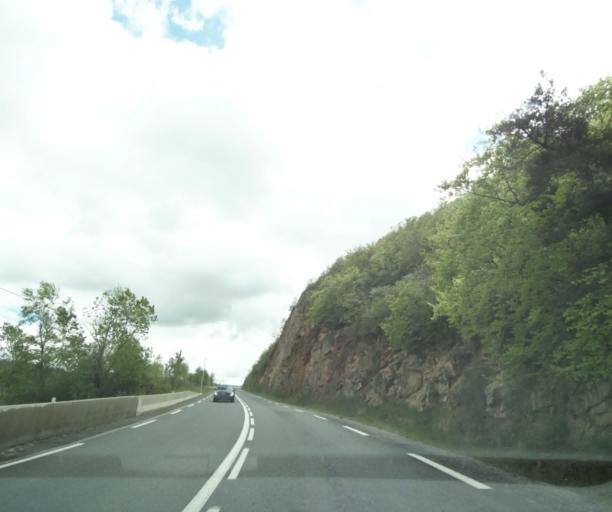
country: FR
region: Midi-Pyrenees
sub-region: Departement de l'Aveyron
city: Millau
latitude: 44.0897
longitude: 3.1246
